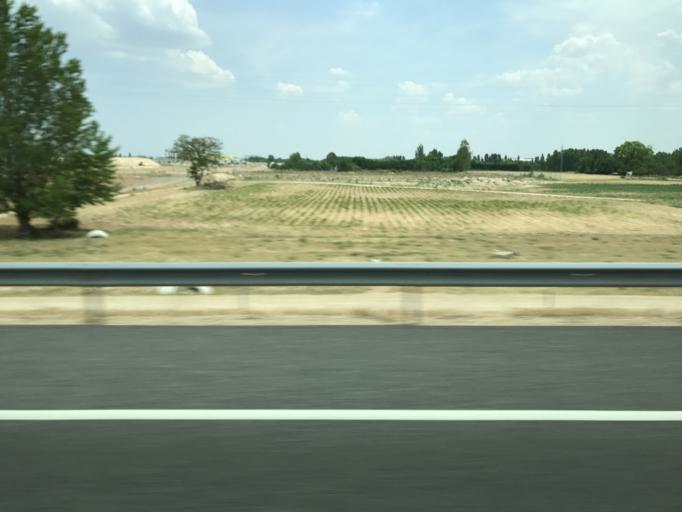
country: ES
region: Castille and Leon
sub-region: Provincia de Burgos
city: Villalba de Duero
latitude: 41.6694
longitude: -3.7281
